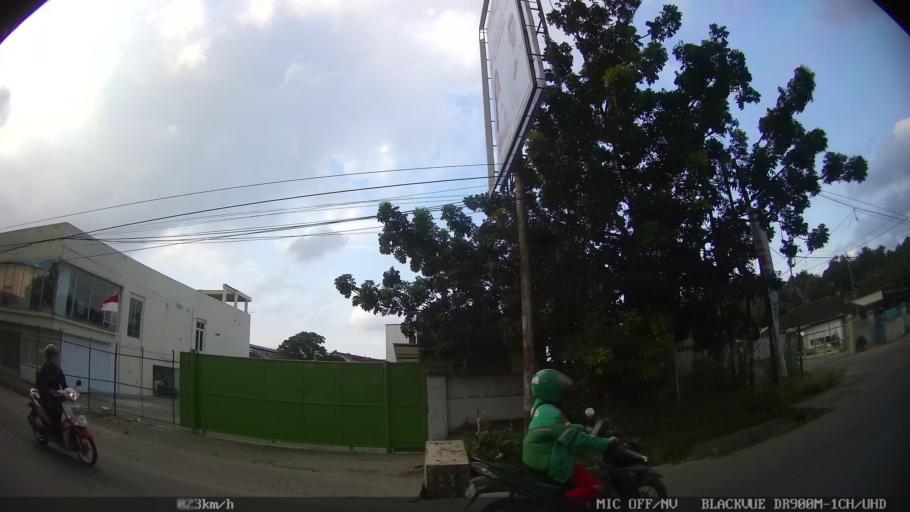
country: ID
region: North Sumatra
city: Medan
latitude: 3.5968
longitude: 98.7437
